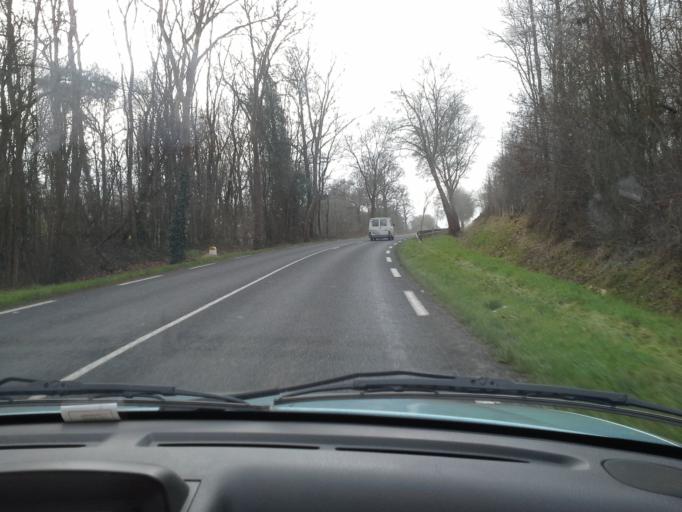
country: FR
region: Centre
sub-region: Departement d'Indre-et-Loire
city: Villedomer
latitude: 47.5457
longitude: 0.8614
